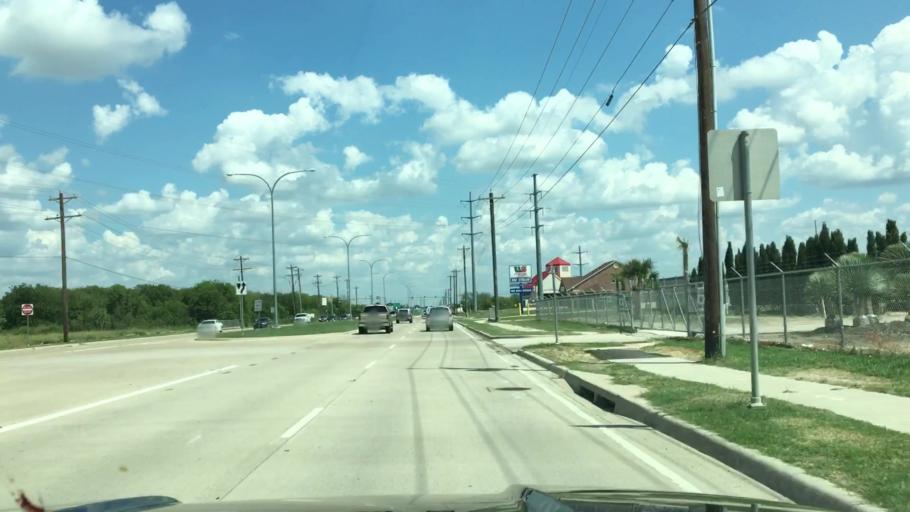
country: US
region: Texas
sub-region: Tarrant County
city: Keller
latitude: 32.9314
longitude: -97.2847
